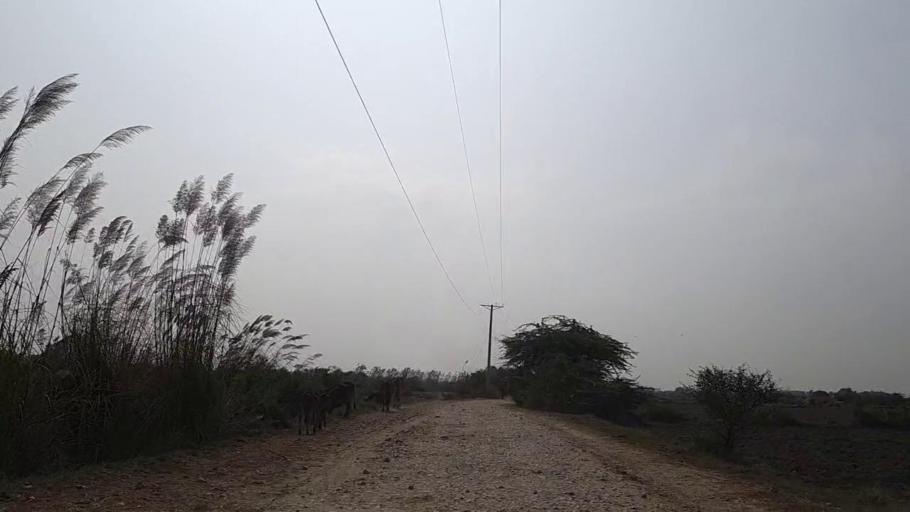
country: PK
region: Sindh
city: Mirpur Sakro
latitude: 24.6322
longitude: 67.7471
